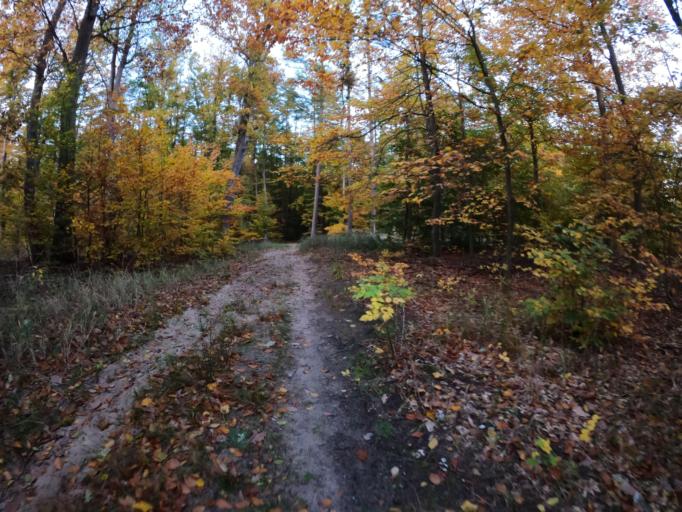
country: PL
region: West Pomeranian Voivodeship
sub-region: Powiat mysliborski
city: Barlinek
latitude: 52.9762
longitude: 15.2306
